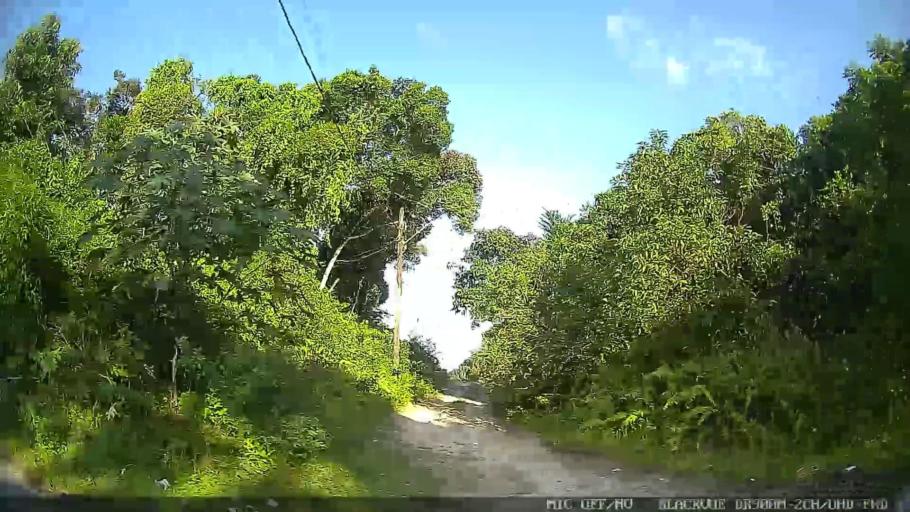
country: BR
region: Sao Paulo
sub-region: Itanhaem
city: Itanhaem
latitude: -24.1503
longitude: -46.8197
